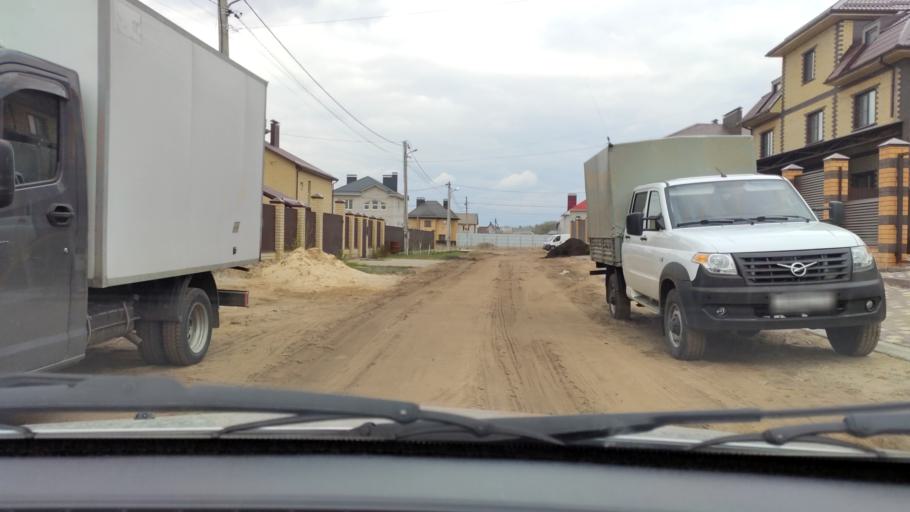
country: RU
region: Voronezj
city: Podgornoye
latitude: 51.7237
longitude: 39.1379
